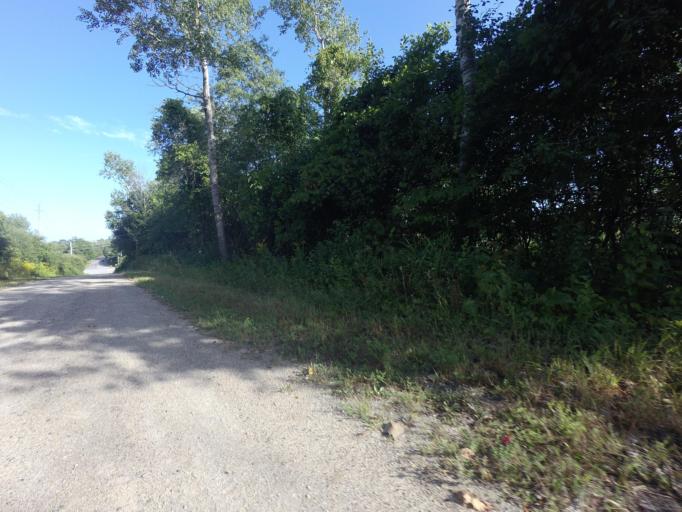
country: CA
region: Ontario
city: Waterloo
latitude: 43.6683
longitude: -80.4400
